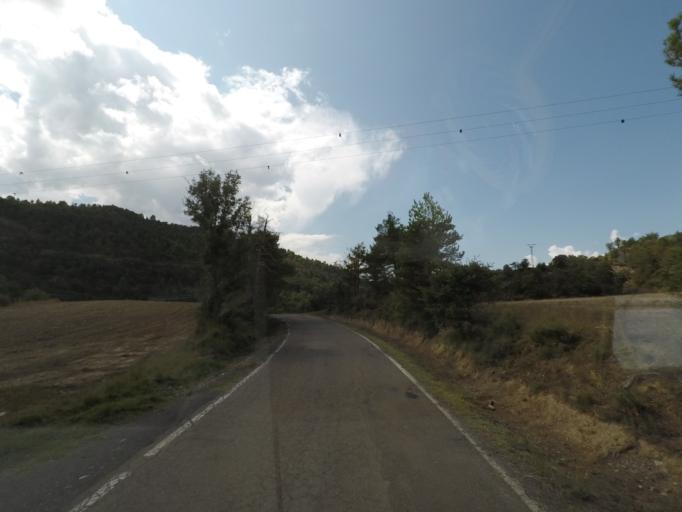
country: ES
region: Aragon
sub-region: Provincia de Huesca
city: Arguis
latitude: 42.4021
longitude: -0.3643
